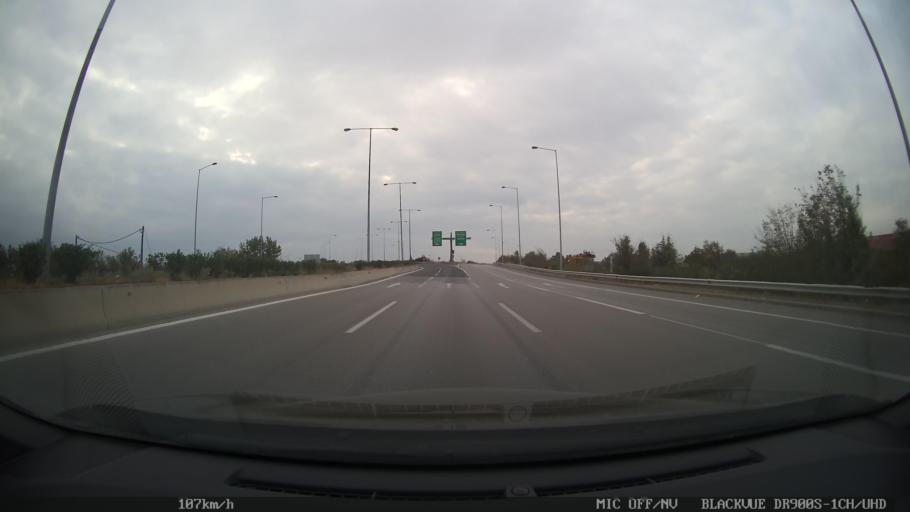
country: GR
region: Central Macedonia
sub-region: Nomos Thessalonikis
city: Kalochori
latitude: 40.6577
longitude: 22.8404
